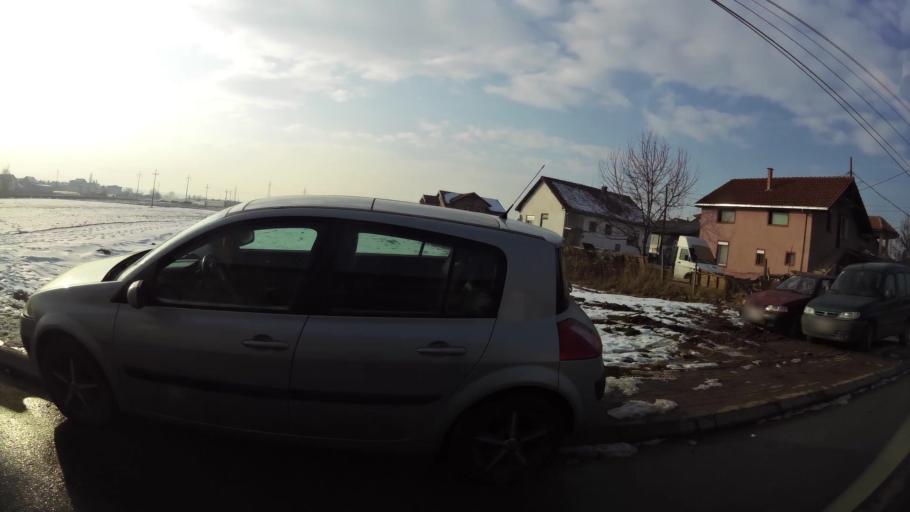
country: MK
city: Creshevo
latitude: 42.0318
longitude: 21.5177
